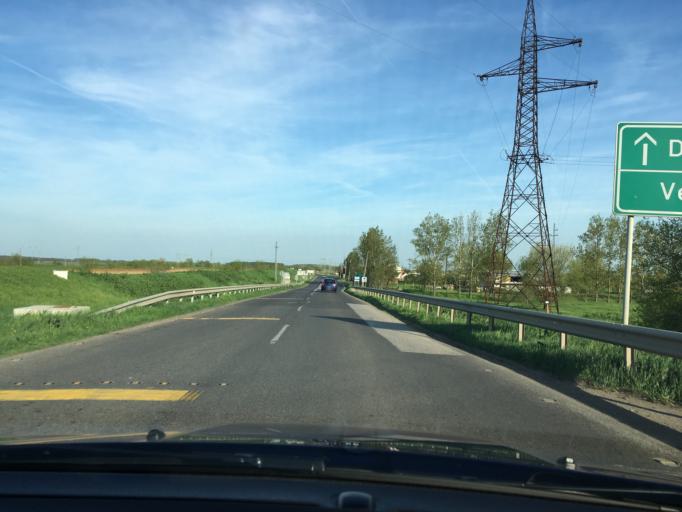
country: HU
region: Bekes
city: Szeghalom
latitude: 47.0130
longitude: 21.1797
